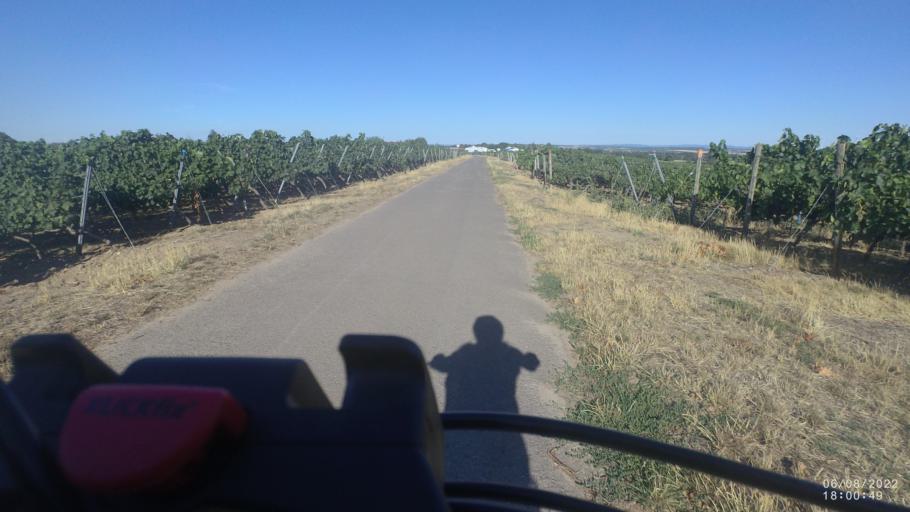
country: DE
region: Rheinland-Pfalz
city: Schornsheim
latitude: 49.8412
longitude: 8.1651
